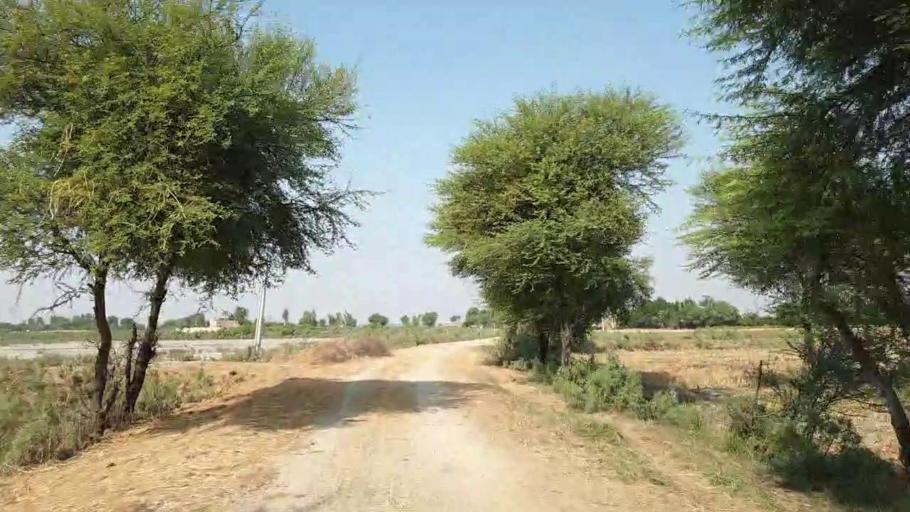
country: PK
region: Sindh
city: Tando Muhammad Khan
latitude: 25.0323
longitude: 68.4044
